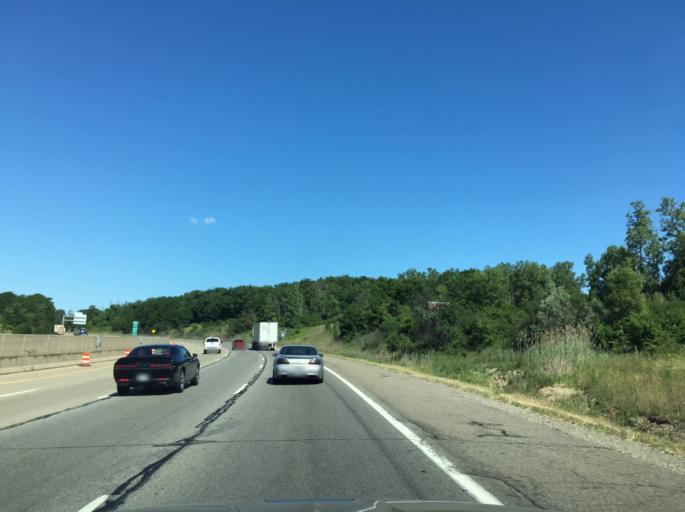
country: US
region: Michigan
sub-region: Oakland County
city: Auburn Hills
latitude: 42.6950
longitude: -83.2540
